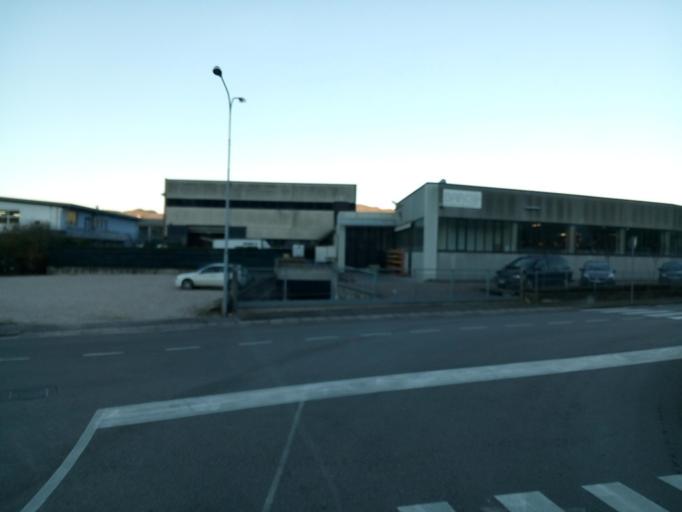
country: IT
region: Veneto
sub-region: Provincia di Vicenza
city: Trissino
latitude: 45.5567
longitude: 11.3824
